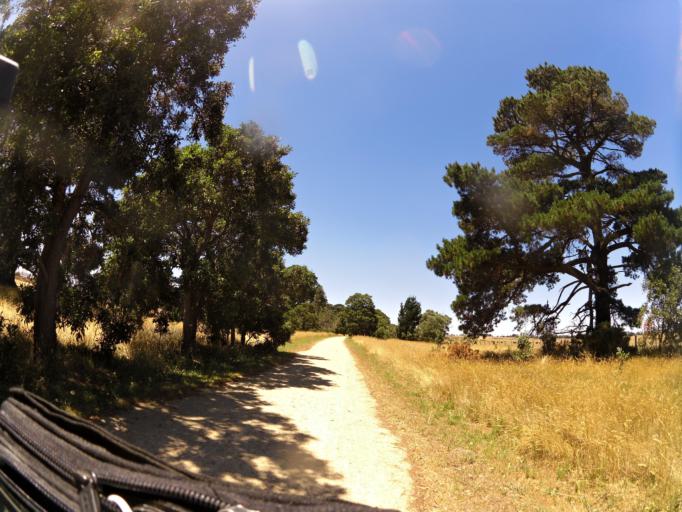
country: AU
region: Victoria
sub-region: Ballarat North
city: Newington
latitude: -37.5315
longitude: 143.7877
